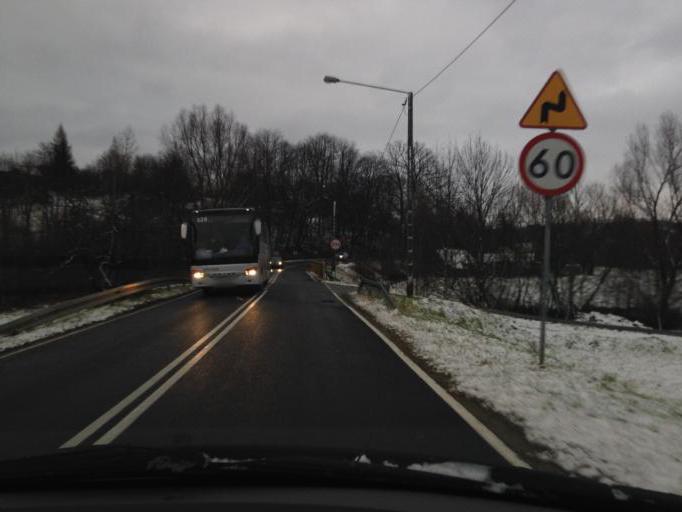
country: PL
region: Lesser Poland Voivodeship
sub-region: Powiat tarnowski
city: Gromnik
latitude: 49.8337
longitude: 20.9958
